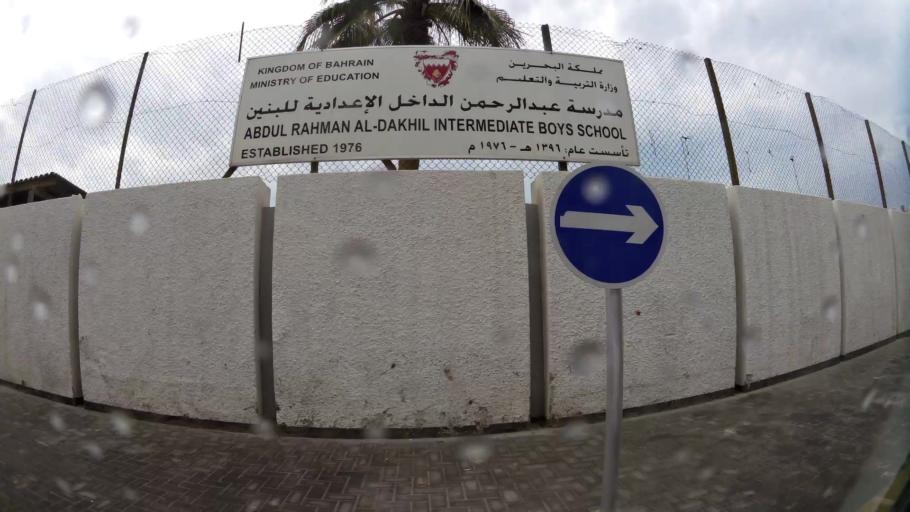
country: BH
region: Manama
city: Manama
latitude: 26.2286
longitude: 50.5939
